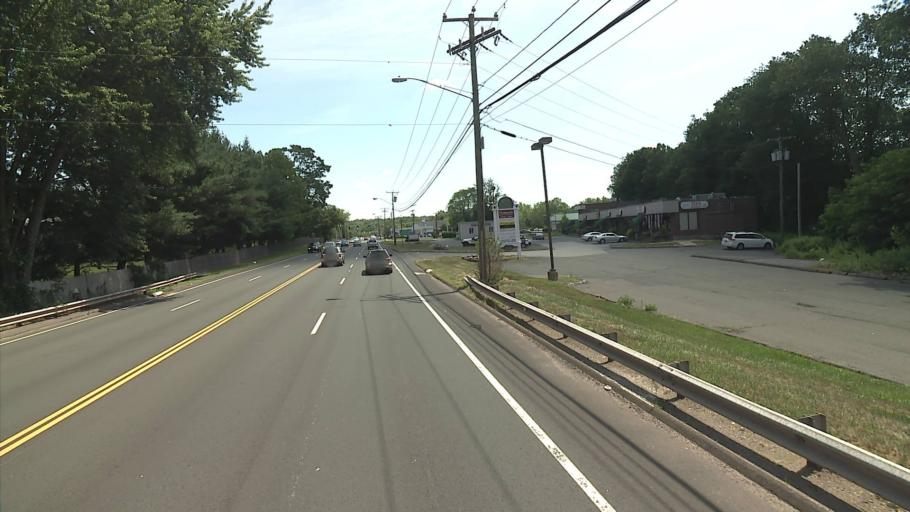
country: US
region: Connecticut
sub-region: Middlesex County
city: Cromwell
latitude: 41.6023
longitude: -72.6842
